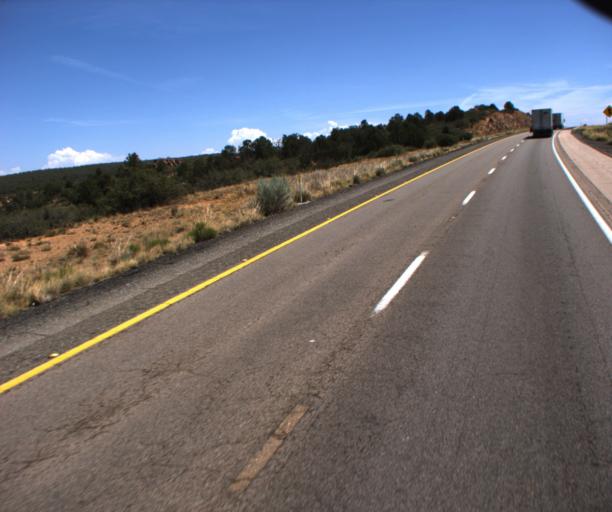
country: US
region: Arizona
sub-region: Mohave County
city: Peach Springs
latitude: 35.2062
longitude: -113.2948
